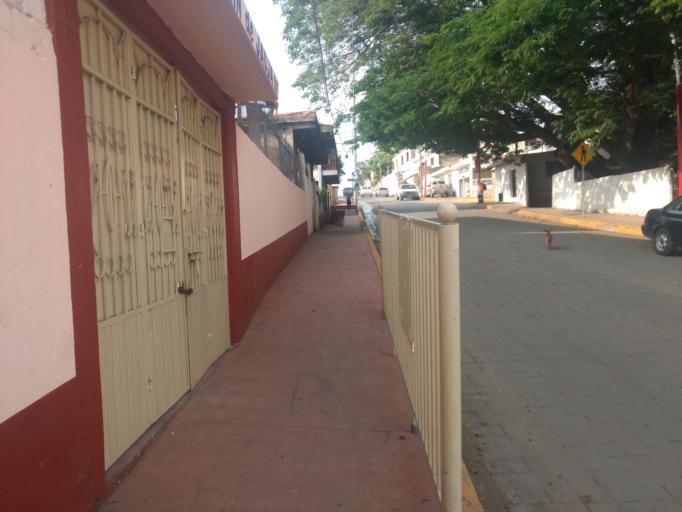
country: MX
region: Nayarit
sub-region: Tepic
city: La Corregidora
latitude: 21.4640
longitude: -104.8014
